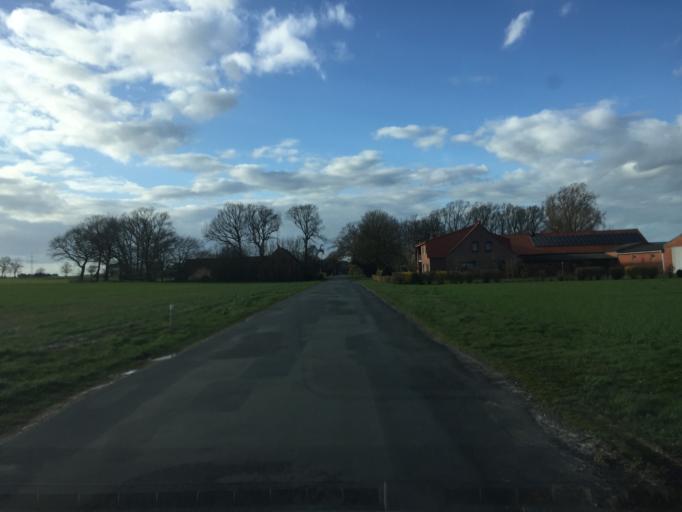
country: DE
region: Lower Saxony
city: Uchte
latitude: 52.5511
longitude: 8.9354
